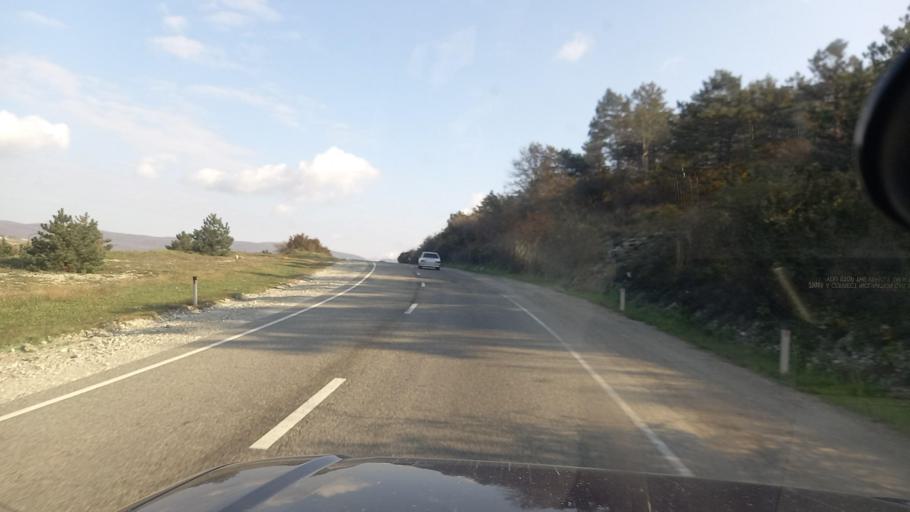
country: RU
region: Krasnodarskiy
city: Verkhnebakanskiy
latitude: 44.8293
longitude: 37.6521
